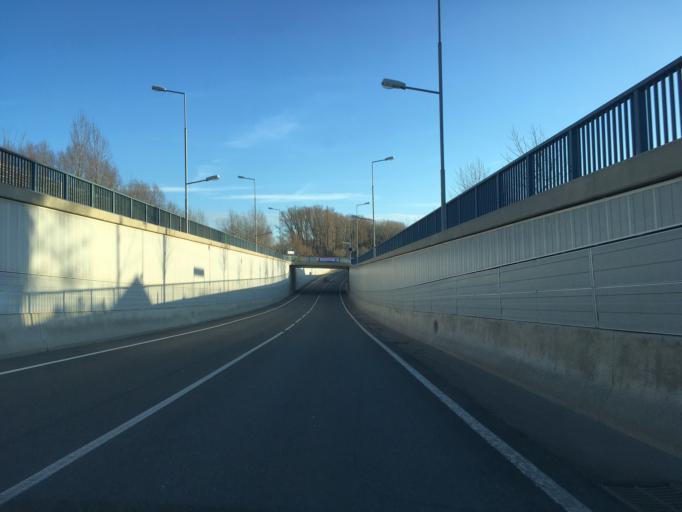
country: AT
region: Lower Austria
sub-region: Politischer Bezirk Wien-Umgebung
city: Klosterneuburg
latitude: 48.3111
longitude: 16.3255
